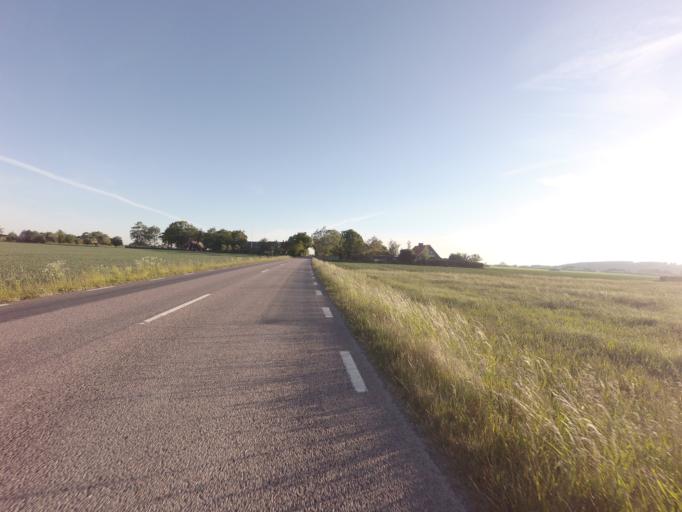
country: SE
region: Skane
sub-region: Helsingborg
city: Odakra
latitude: 56.1574
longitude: 12.6788
